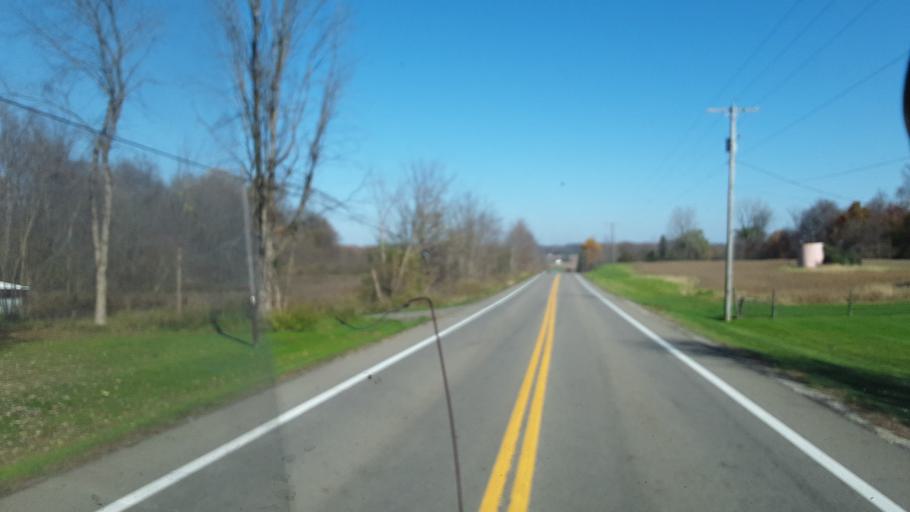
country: US
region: Ohio
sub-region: Knox County
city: Fredericktown
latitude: 40.5081
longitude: -82.6739
